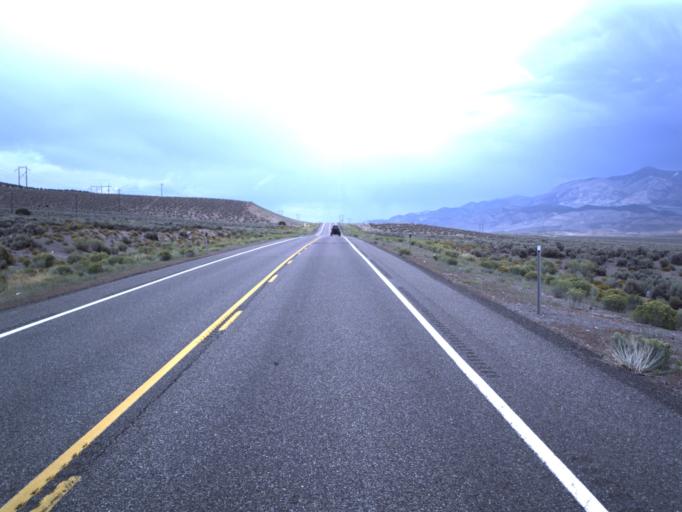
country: US
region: Utah
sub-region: Piute County
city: Junction
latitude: 38.3115
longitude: -112.2220
